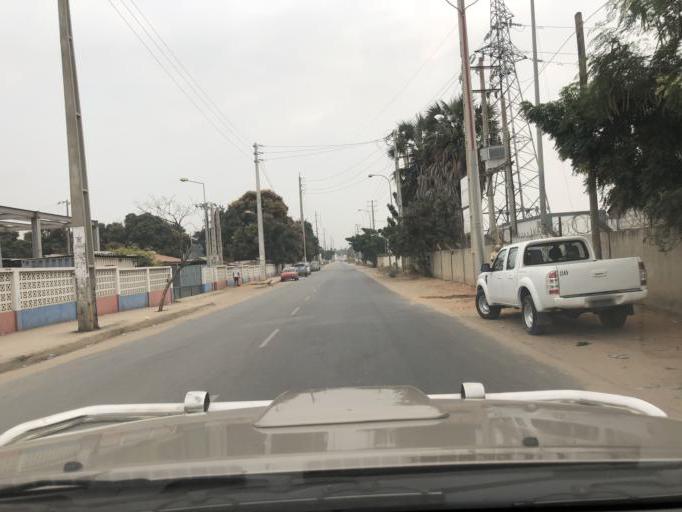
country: AO
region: Luanda
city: Luanda
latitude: -8.8926
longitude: 13.1886
